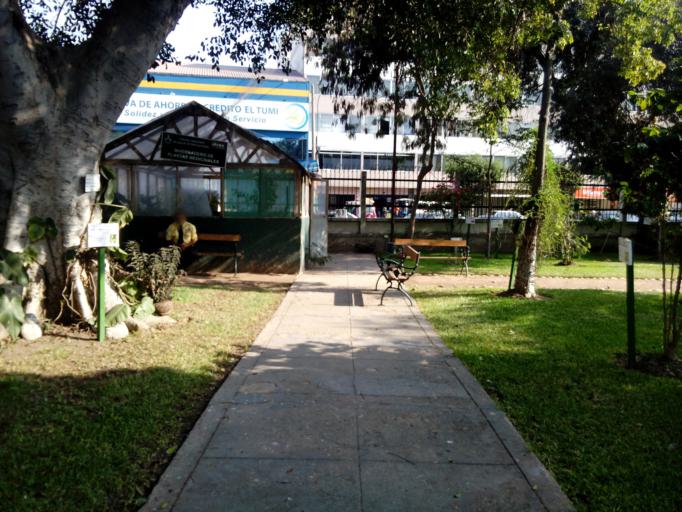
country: PE
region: Lima
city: Lima
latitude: -12.0735
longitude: -77.0412
